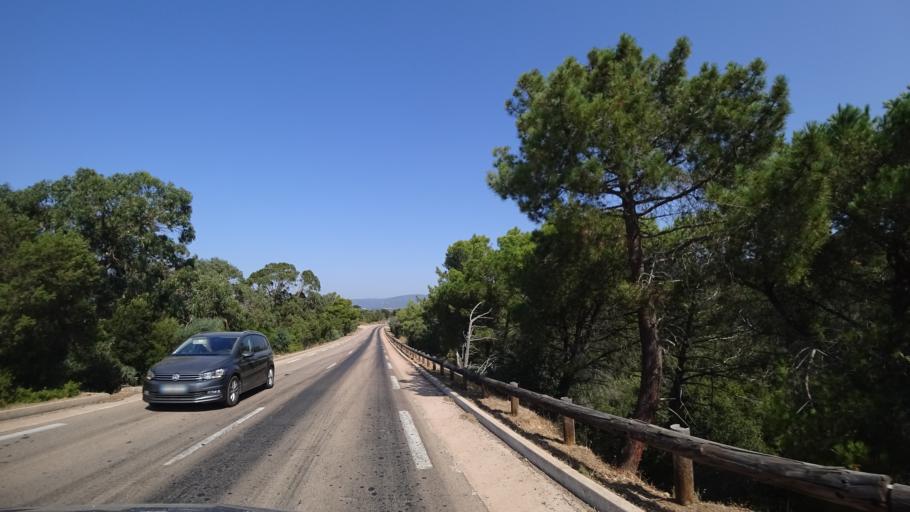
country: FR
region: Corsica
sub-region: Departement de la Corse-du-Sud
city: Bonifacio
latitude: 41.4716
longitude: 9.0941
